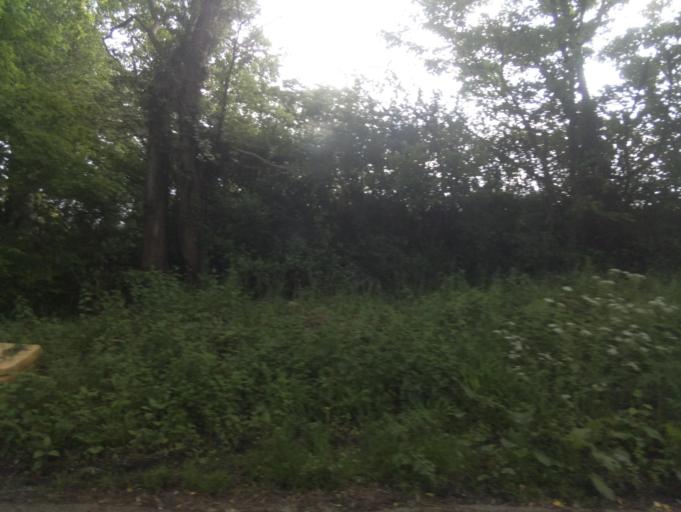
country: GB
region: England
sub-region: Wiltshire
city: Malmesbury
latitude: 51.5492
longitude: -2.0890
